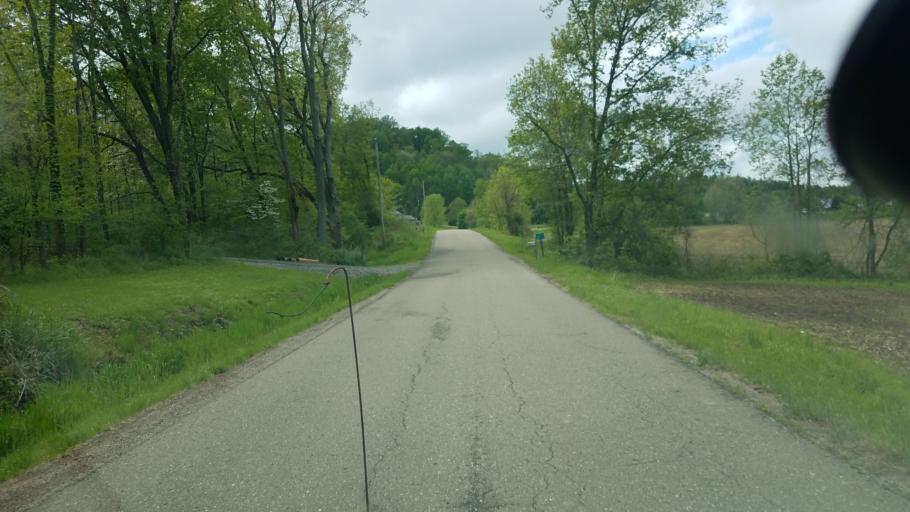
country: US
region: Ohio
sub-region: Tuscarawas County
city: Dover
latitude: 40.5822
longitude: -81.4013
